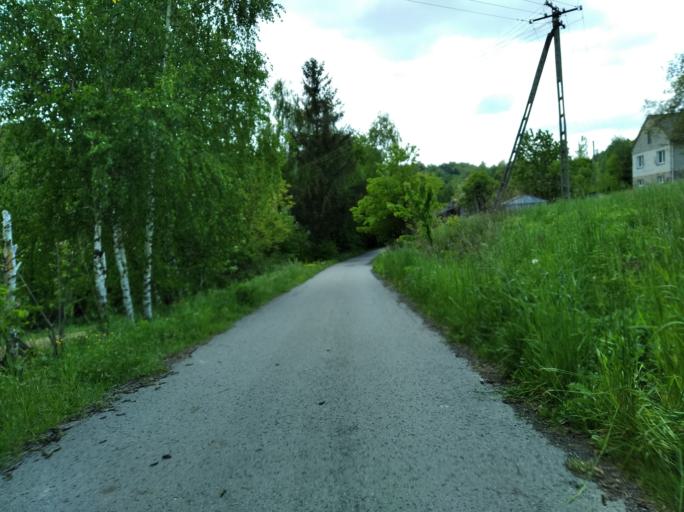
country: PL
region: Subcarpathian Voivodeship
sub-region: Powiat ropczycko-sedziszowski
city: Wielopole Skrzynskie
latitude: 49.9253
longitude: 21.6224
